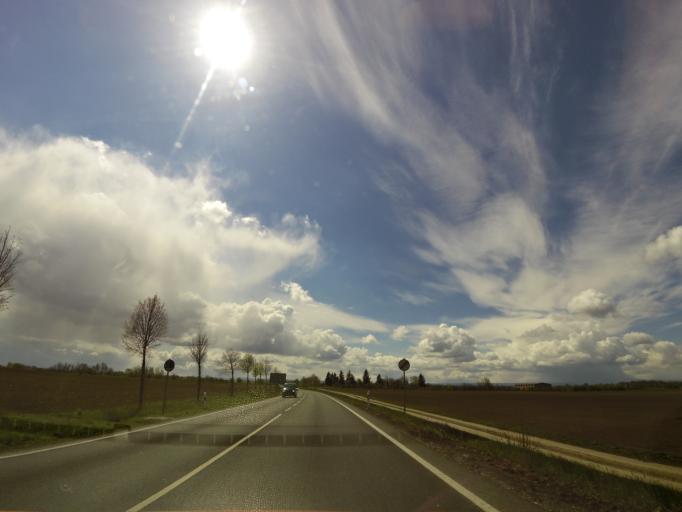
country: DE
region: Saxony-Anhalt
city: Groeningen
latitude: 51.9412
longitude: 11.1890
